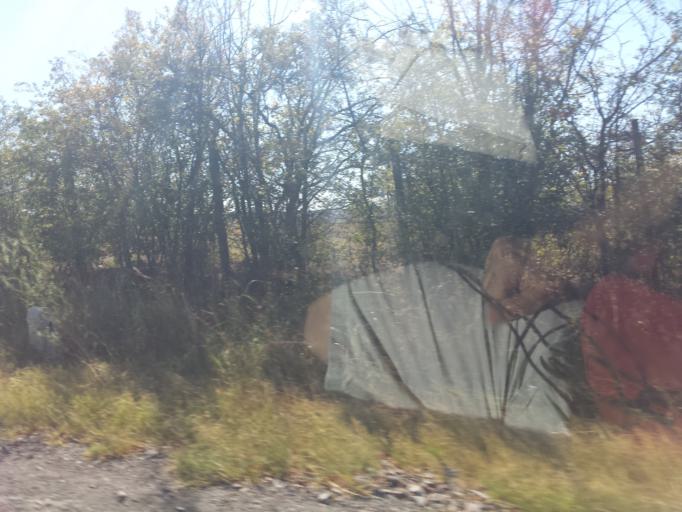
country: RO
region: Tulcea
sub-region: Municipiul Tulcea
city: Tulcea
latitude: 45.1530
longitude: 28.7859
